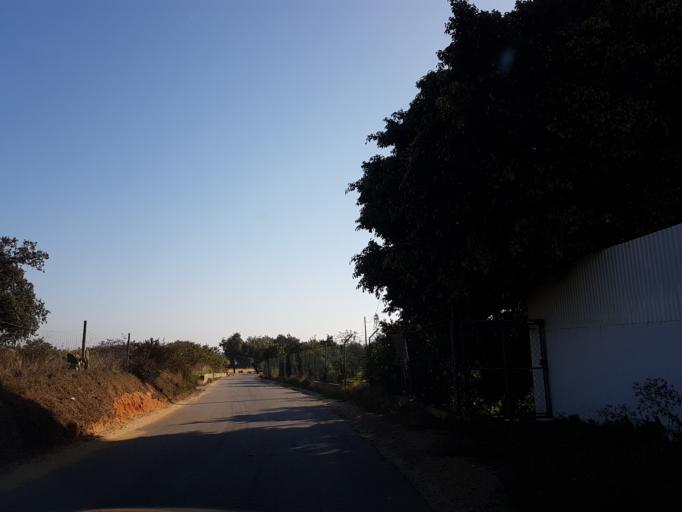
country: PT
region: Faro
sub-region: Albufeira
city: Ferreiras
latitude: 37.0999
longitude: -8.2055
